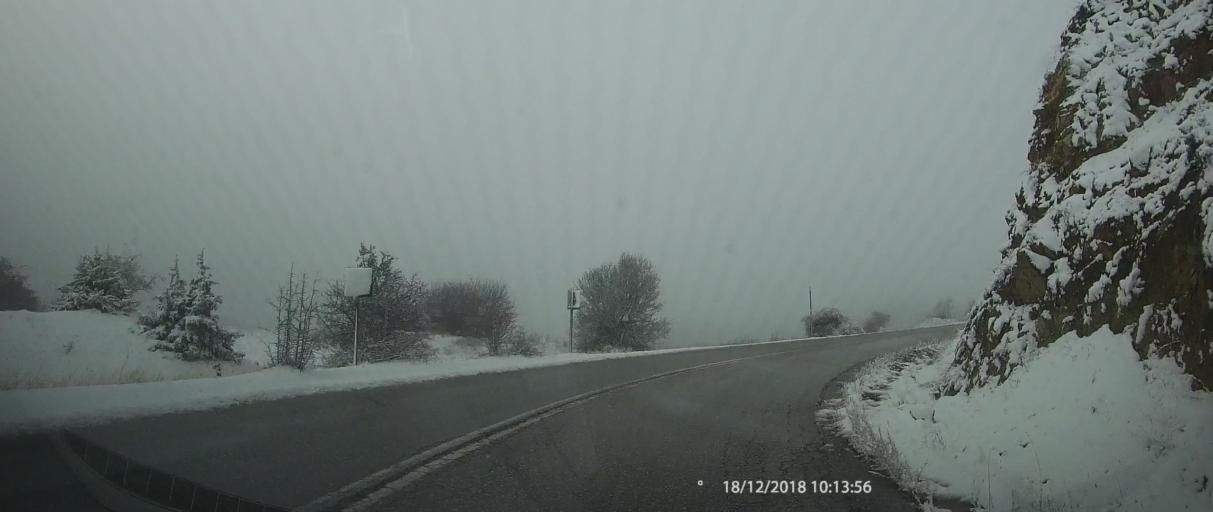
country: GR
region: Thessaly
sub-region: Nomos Larisis
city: Livadi
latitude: 40.1058
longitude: 22.2065
